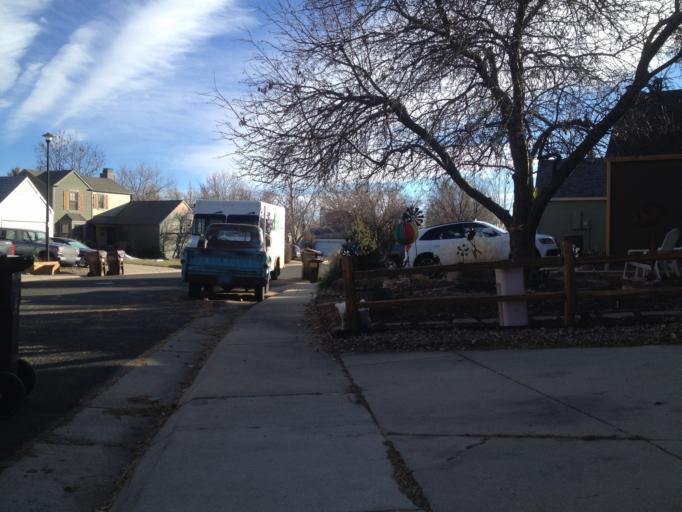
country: US
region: Colorado
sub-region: Boulder County
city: Louisville
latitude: 39.9736
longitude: -105.1491
